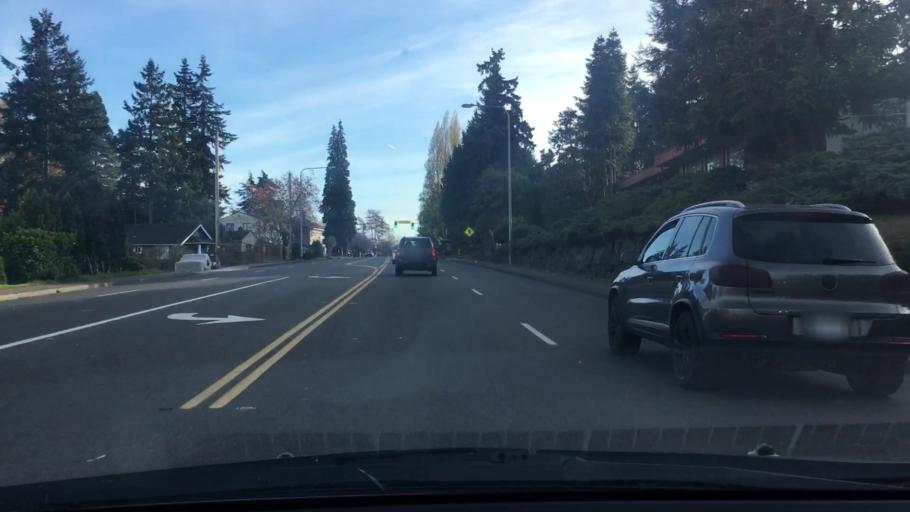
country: US
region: Washington
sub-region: King County
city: Burien
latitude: 47.4866
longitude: -122.3497
